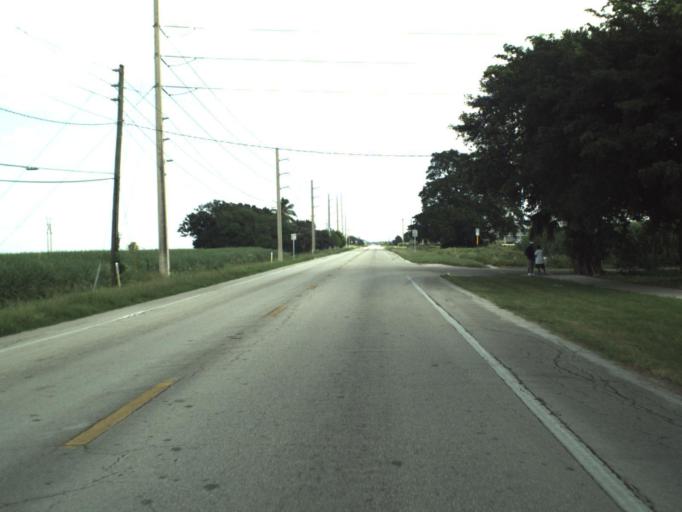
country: US
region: Florida
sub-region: Palm Beach County
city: Belle Glade
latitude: 26.6999
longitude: -80.6840
